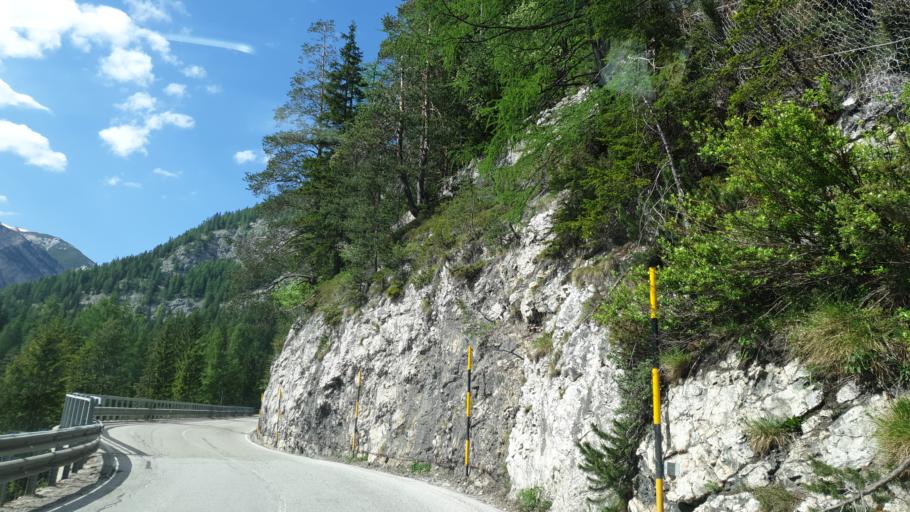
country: IT
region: Veneto
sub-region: Provincia di Belluno
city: Cortina d'Ampezzo
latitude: 46.5991
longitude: 12.1091
